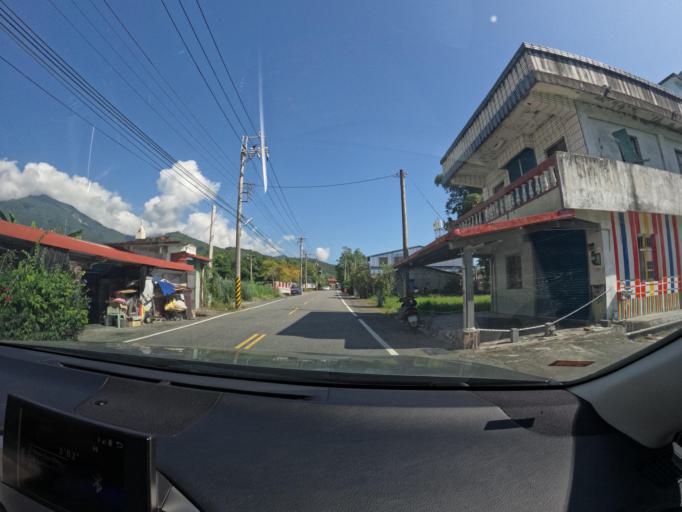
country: TW
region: Taiwan
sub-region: Hualien
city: Hualian
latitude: 23.5713
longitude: 121.3740
